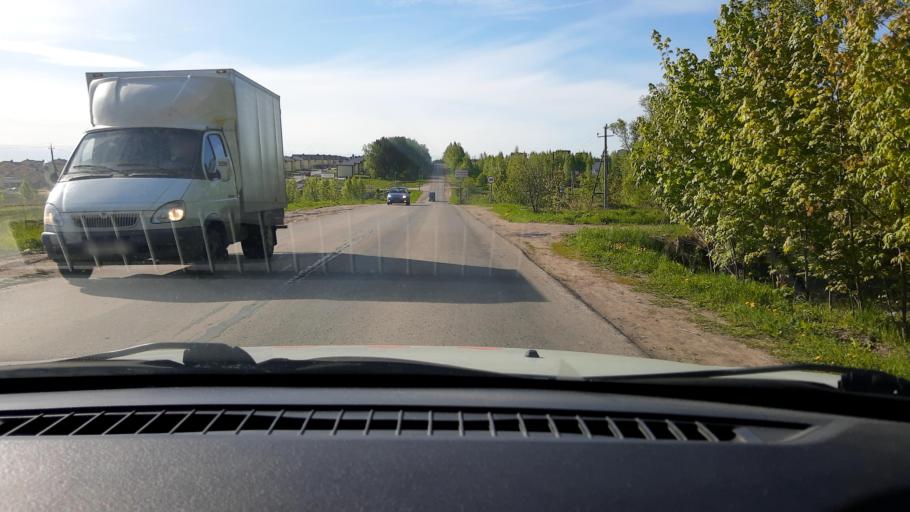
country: RU
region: Nizjnij Novgorod
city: Burevestnik
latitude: 56.1696
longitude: 43.7649
